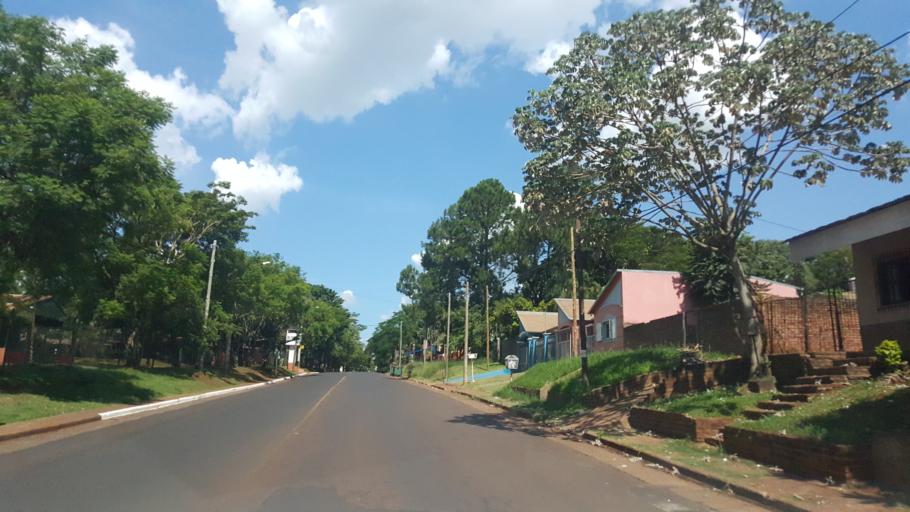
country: AR
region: Misiones
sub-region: Departamento de Capital
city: Posadas
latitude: -27.3648
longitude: -55.9236
